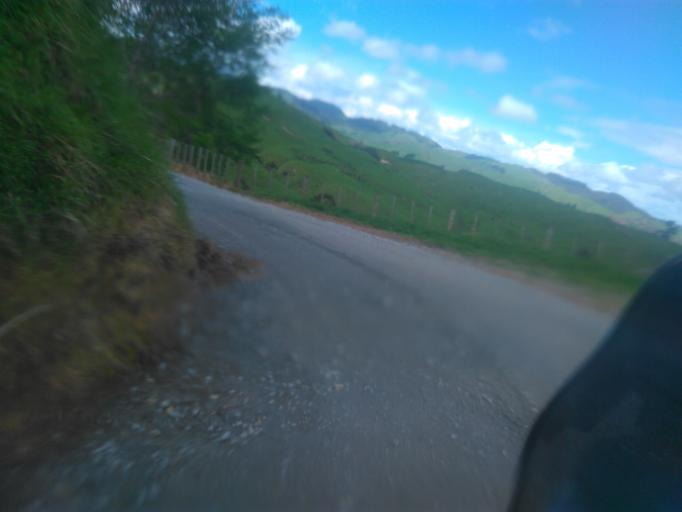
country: NZ
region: Hawke's Bay
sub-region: Wairoa District
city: Wairoa
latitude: -38.7778
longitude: 177.6296
